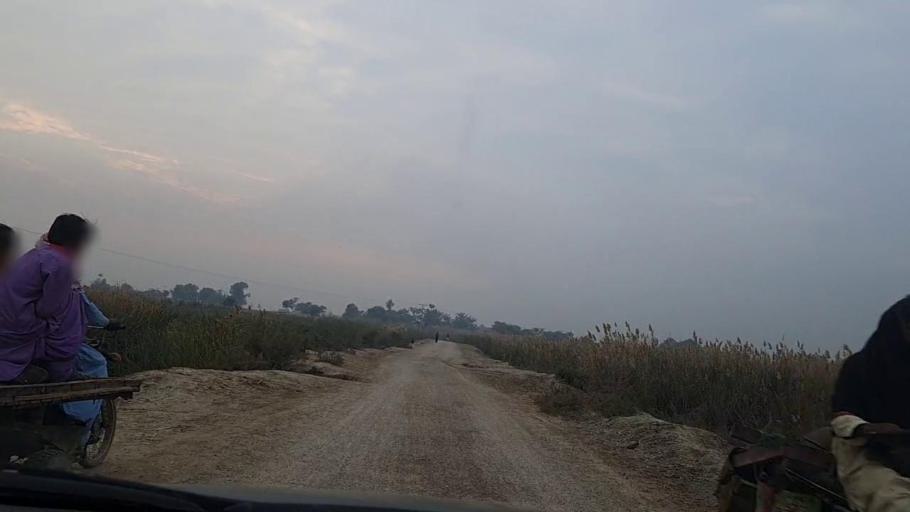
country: PK
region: Sindh
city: Sakrand
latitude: 26.2905
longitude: 68.2480
